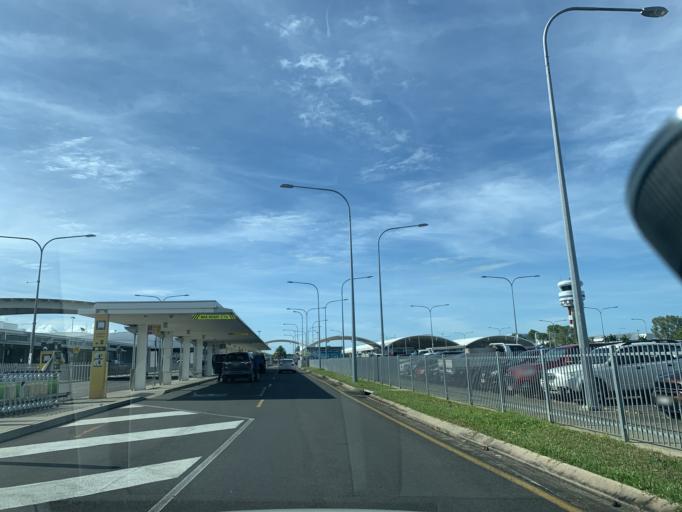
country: AU
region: Queensland
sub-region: Cairns
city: Cairns
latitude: -16.8779
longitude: 145.7548
